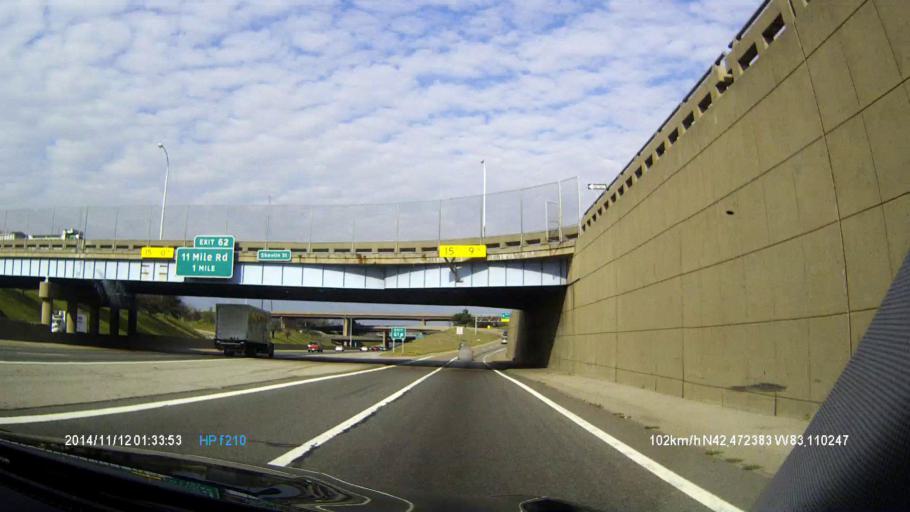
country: US
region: Michigan
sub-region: Oakland County
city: Hazel Park
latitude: 42.4724
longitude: -83.1103
